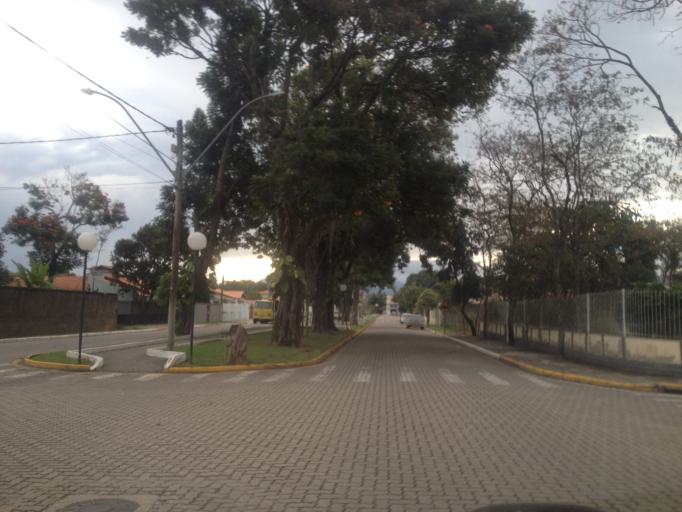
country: BR
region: Rio de Janeiro
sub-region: Porto Real
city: Porto Real
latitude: -22.4201
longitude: -44.2931
